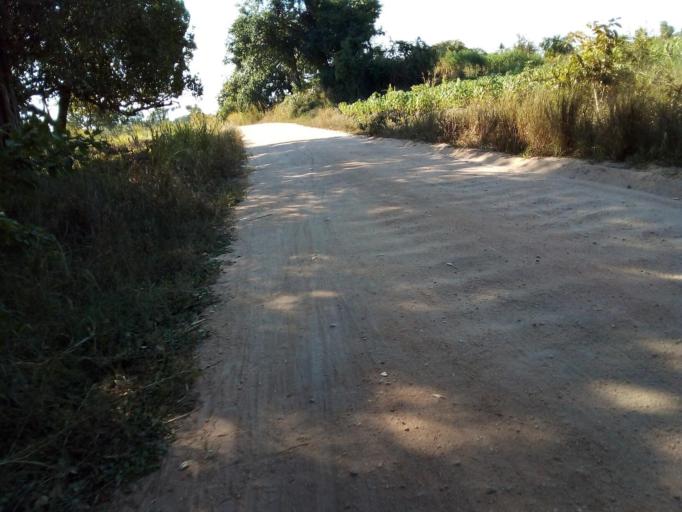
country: MZ
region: Zambezia
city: Quelimane
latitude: -17.5312
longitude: 36.6197
